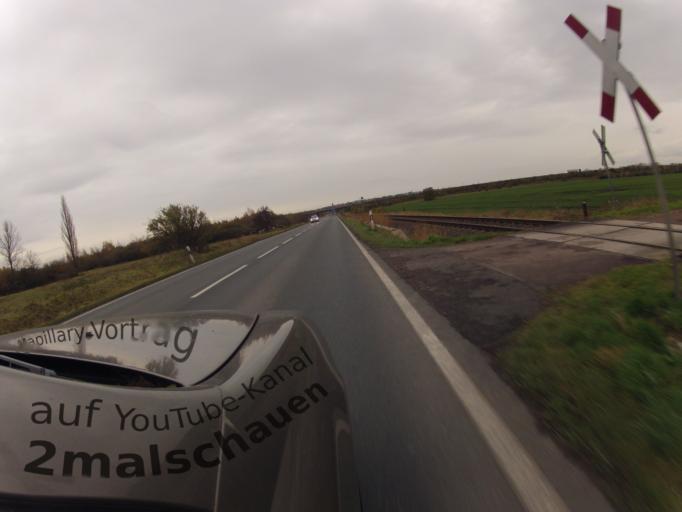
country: DE
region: Saxony-Anhalt
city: Konnern
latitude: 51.6877
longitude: 11.7673
